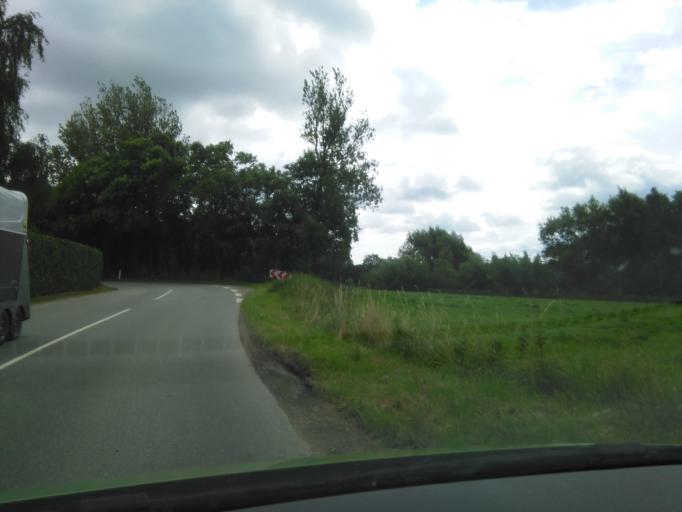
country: DK
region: Central Jutland
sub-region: Arhus Kommune
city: Logten
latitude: 56.2499
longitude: 10.3217
